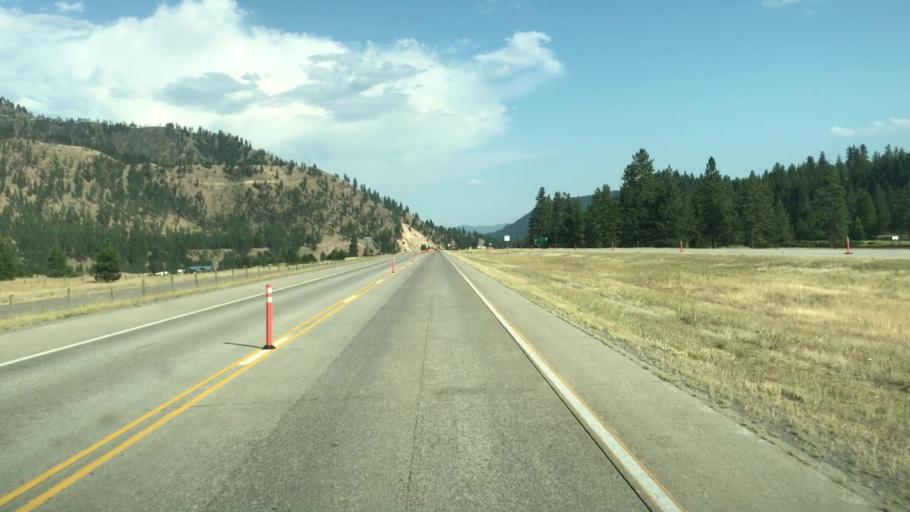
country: US
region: Montana
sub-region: Mineral County
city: Superior
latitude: 47.2305
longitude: -114.9788
